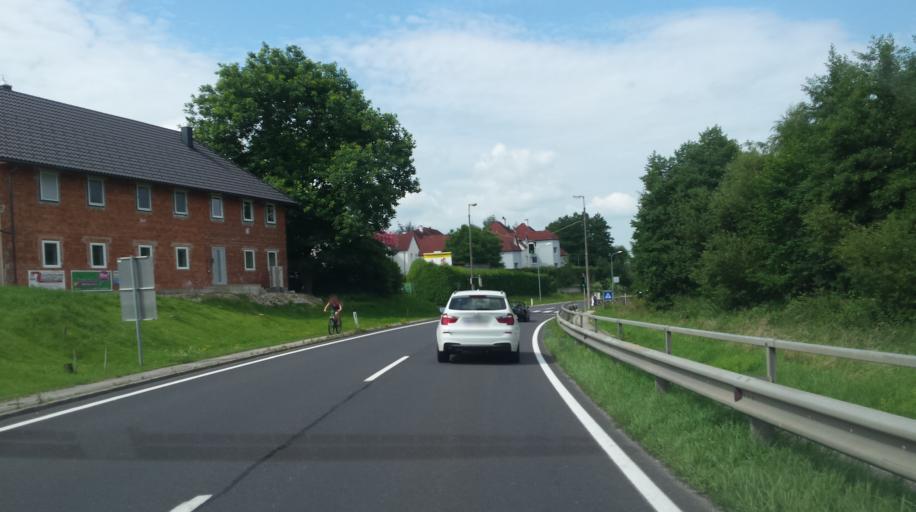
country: AT
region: Lower Austria
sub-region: Politischer Bezirk Amstetten
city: Haag
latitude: 48.1142
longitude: 14.5674
